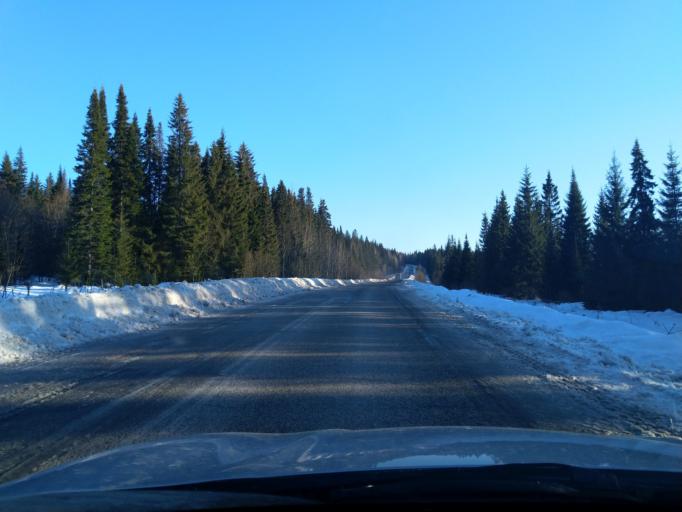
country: RU
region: Perm
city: Polazna
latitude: 58.3055
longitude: 56.4719
